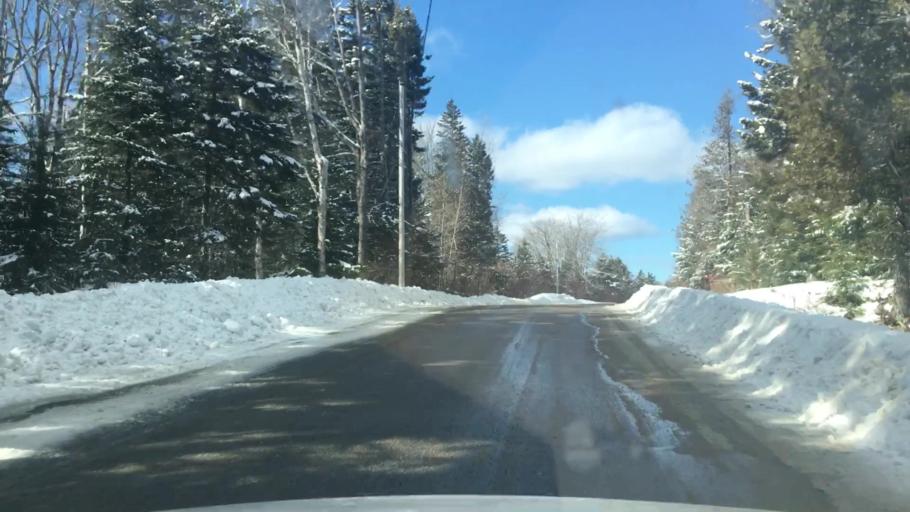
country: US
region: Maine
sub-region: Washington County
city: Machias
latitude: 44.6801
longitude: -67.4549
